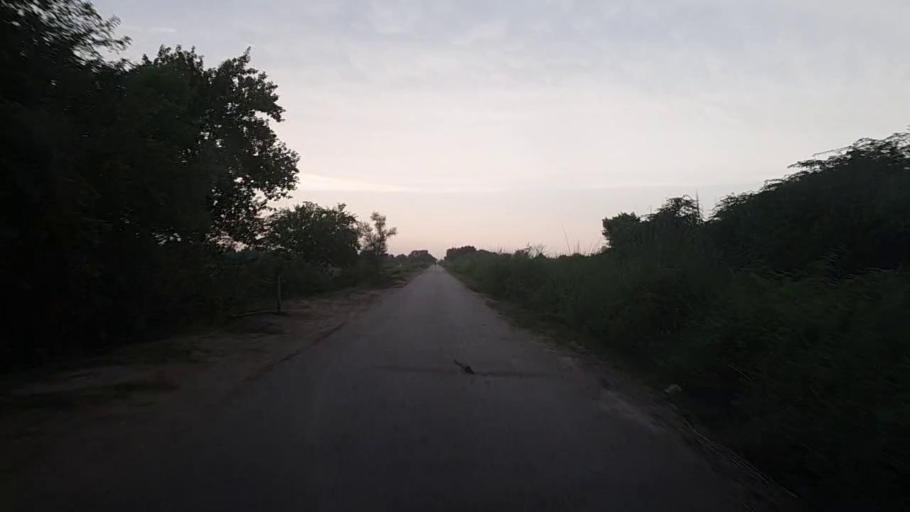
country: PK
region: Sindh
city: Karaundi
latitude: 27.0170
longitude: 68.3525
